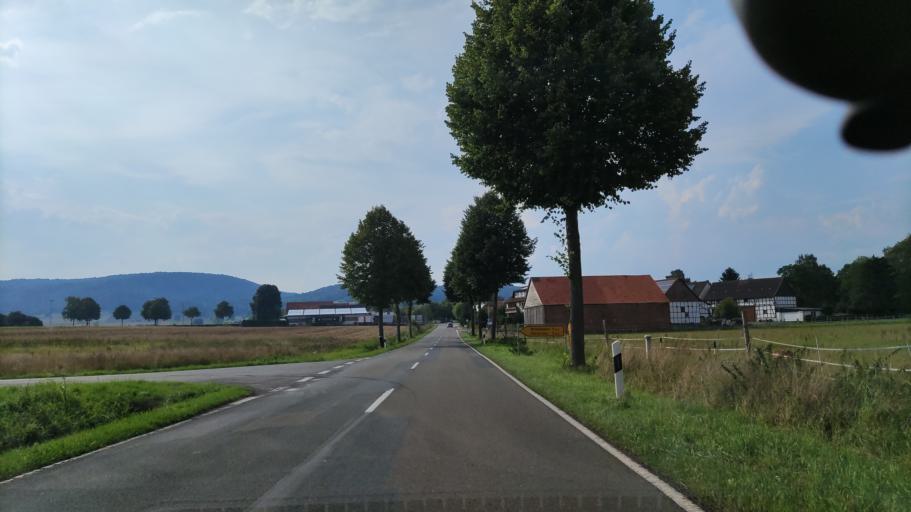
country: DE
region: Lower Saxony
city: Wangelnstedt
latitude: 51.8422
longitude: 9.7284
